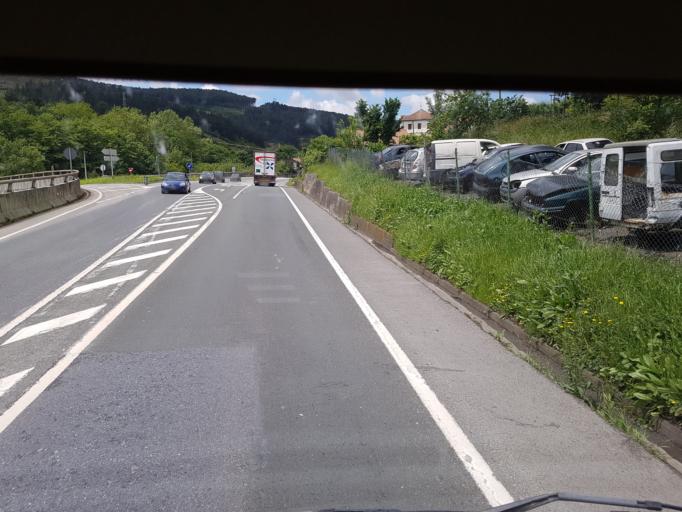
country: ES
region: Basque Country
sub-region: Bizkaia
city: Amorebieta
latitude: 43.2308
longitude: -2.7803
